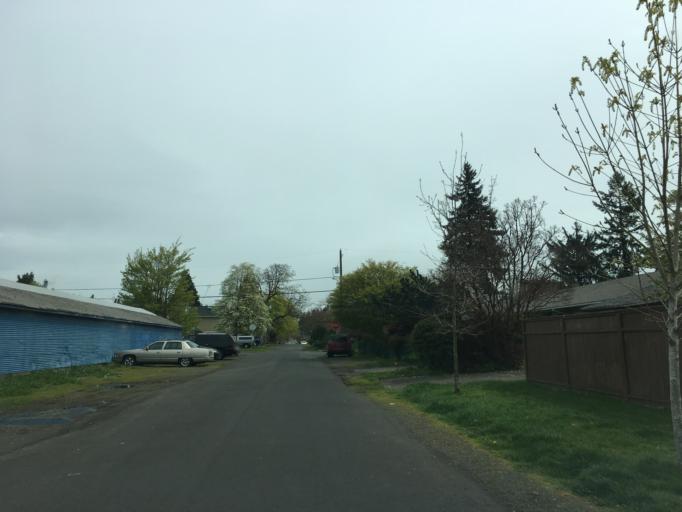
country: US
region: Oregon
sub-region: Multnomah County
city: Lents
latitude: 45.5496
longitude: -122.5846
